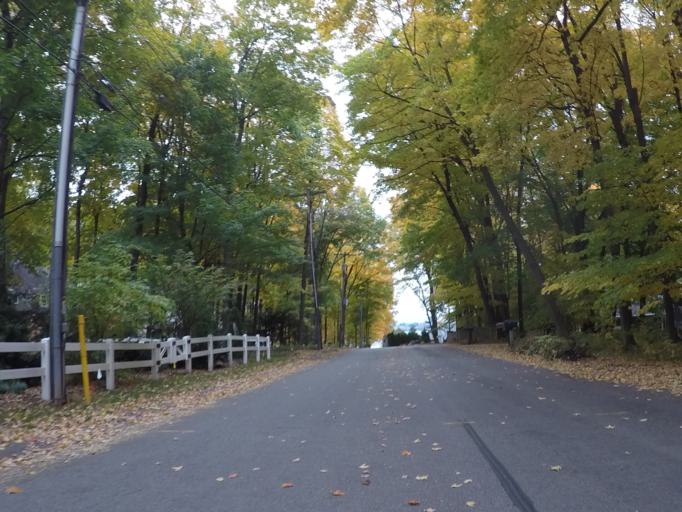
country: US
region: Wisconsin
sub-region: Dane County
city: Maple Bluff
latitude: 43.1154
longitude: -89.3809
